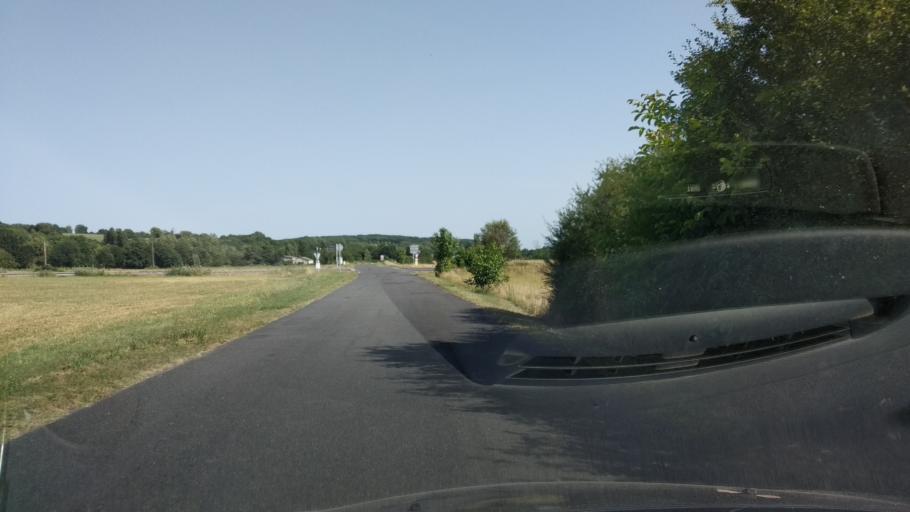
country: FR
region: Poitou-Charentes
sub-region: Departement de la Vienne
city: Lussac-les-Chateaux
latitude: 46.4397
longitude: 0.6712
